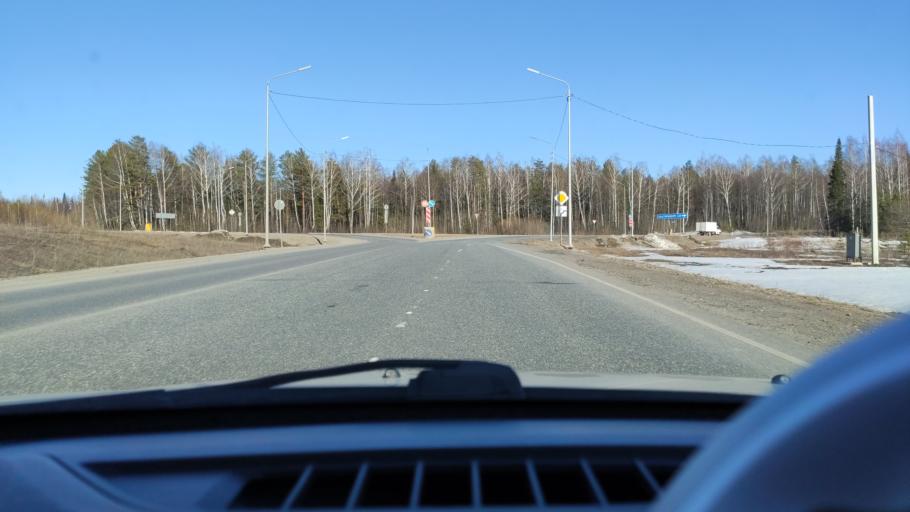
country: RU
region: Perm
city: Suksun
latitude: 57.0924
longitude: 57.3896
